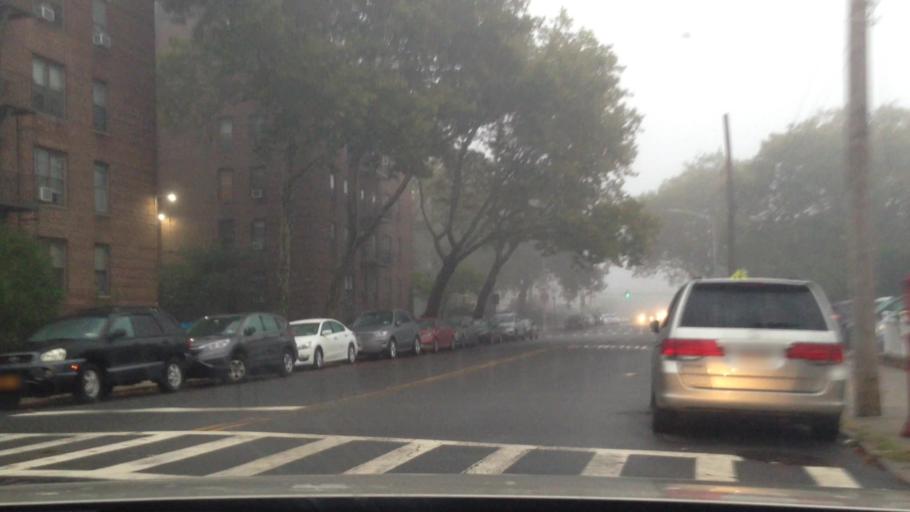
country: US
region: New York
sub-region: Kings County
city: Brooklyn
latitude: 40.5965
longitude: -73.9354
